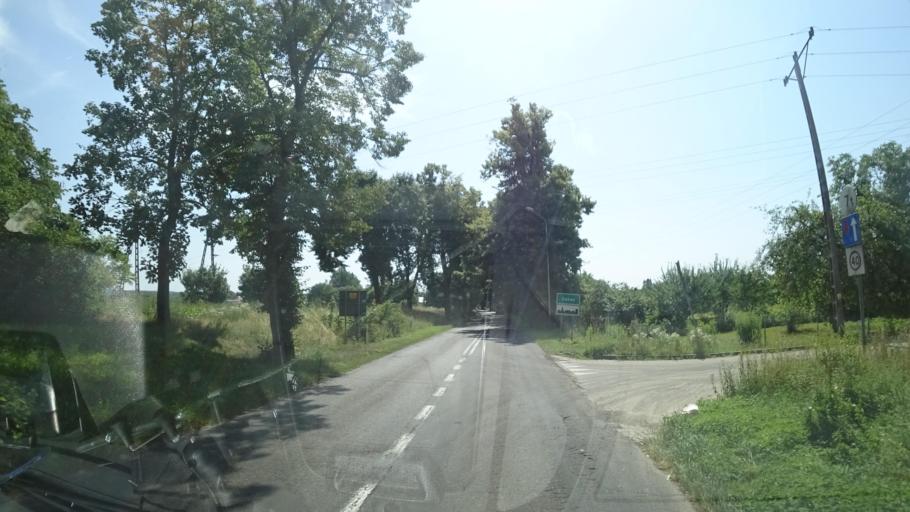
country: PL
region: West Pomeranian Voivodeship
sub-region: Powiat lobeski
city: Lobez
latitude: 53.6499
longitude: 15.6142
